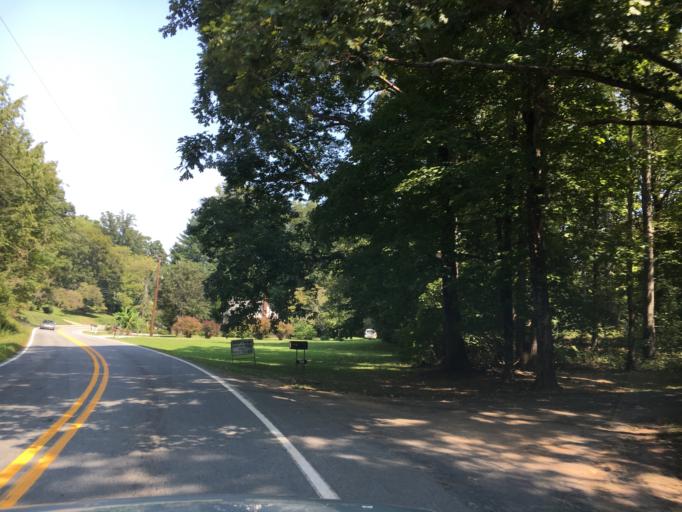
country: US
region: North Carolina
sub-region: McDowell County
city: Marion
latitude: 35.6610
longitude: -81.9641
